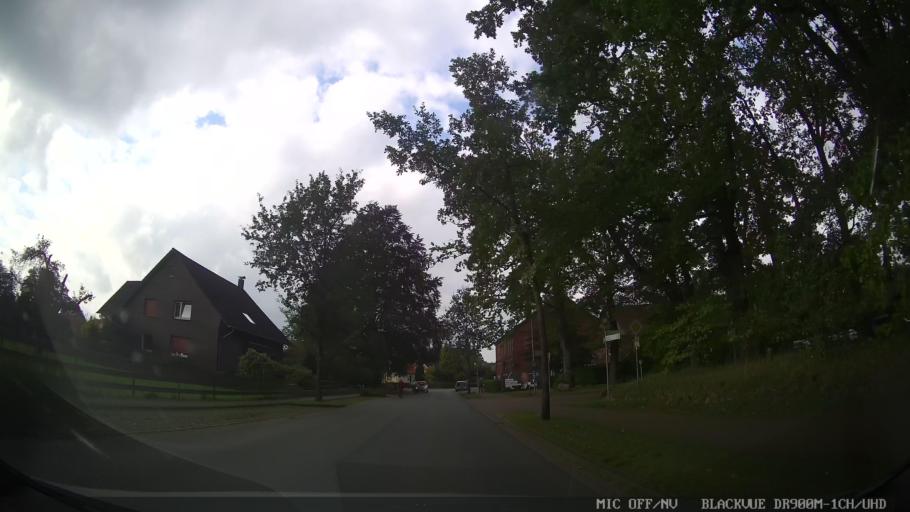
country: DE
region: Lower Saxony
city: Wietzendorf
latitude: 52.9137
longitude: 9.9784
